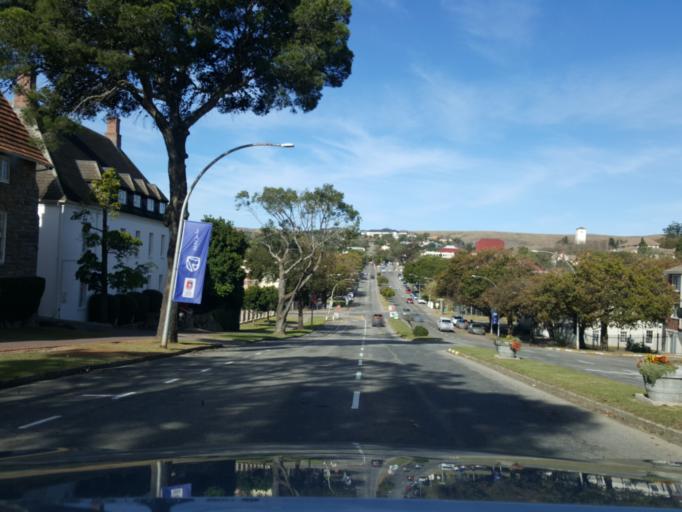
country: ZA
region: Eastern Cape
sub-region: Cacadu District Municipality
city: Grahamstown
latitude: -33.3083
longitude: 26.5188
